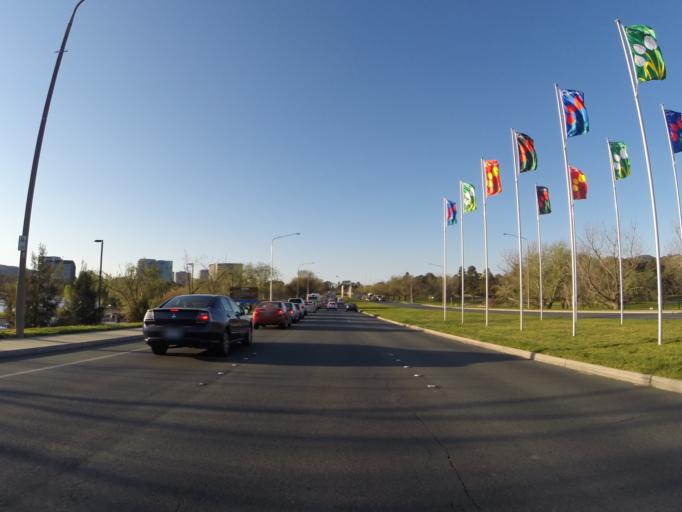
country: AU
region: Australian Capital Territory
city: Canberra
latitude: -35.2912
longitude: 149.1270
